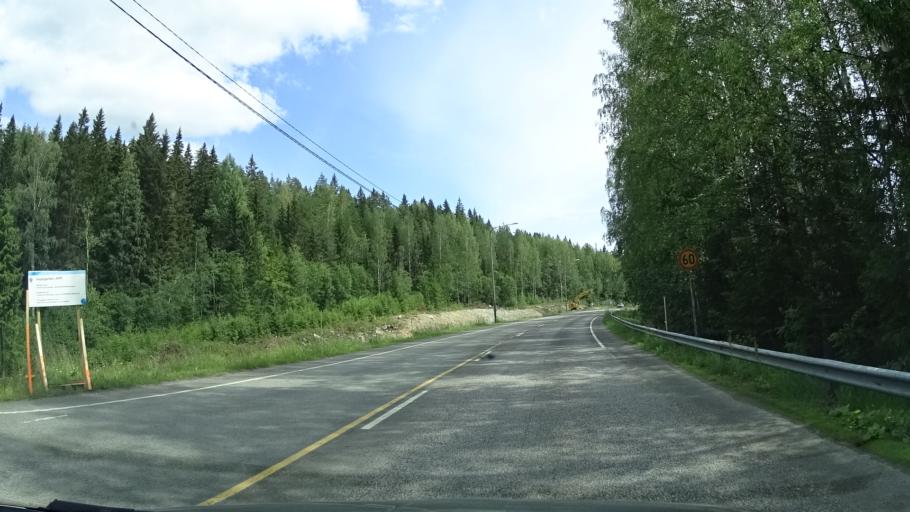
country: FI
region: Central Finland
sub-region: Jyvaeskylae
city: Jyvaeskylae
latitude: 62.2493
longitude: 25.6517
